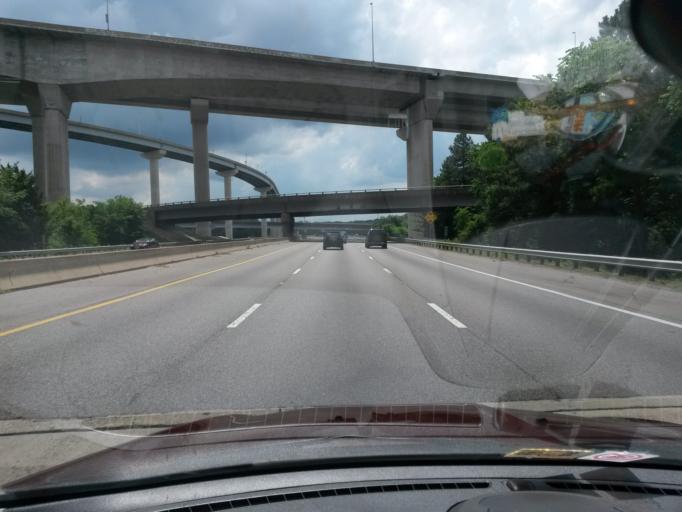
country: US
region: Virginia
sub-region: Chesterfield County
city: Bensley
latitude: 37.4438
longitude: -77.4251
